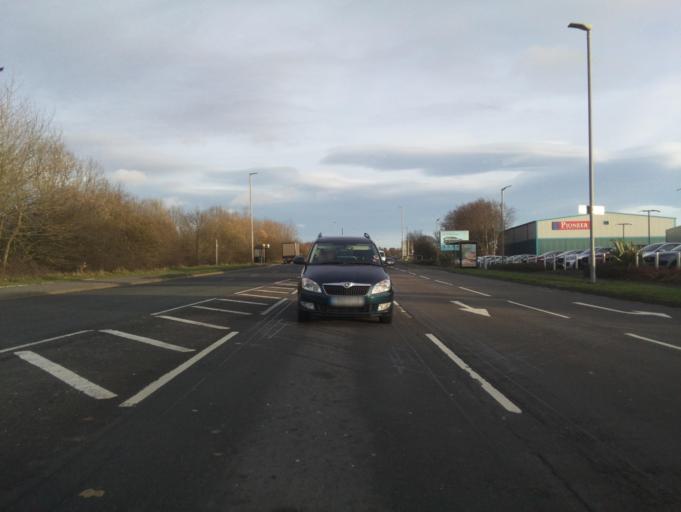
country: GB
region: England
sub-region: Cumbria
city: Scotby
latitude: 54.8955
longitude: -2.8953
